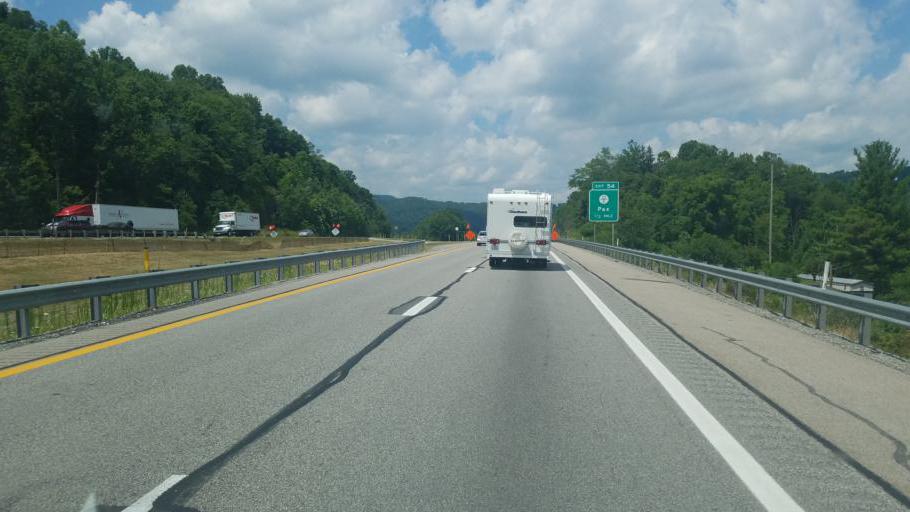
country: US
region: West Virginia
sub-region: Raleigh County
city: Bradley
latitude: 37.9067
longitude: -81.2662
